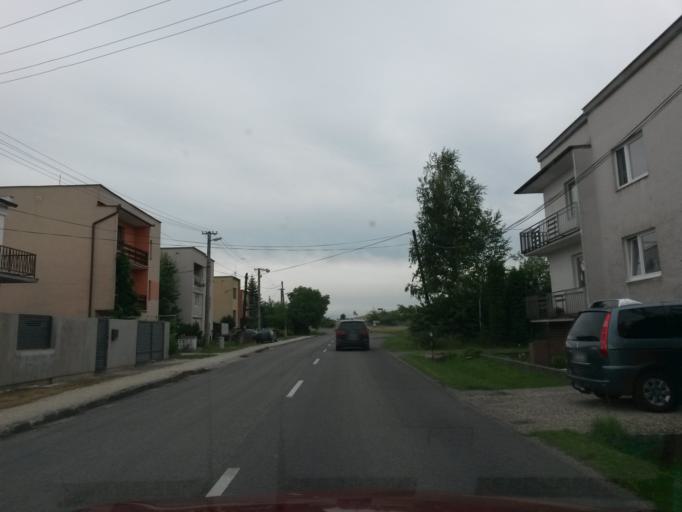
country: SK
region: Banskobystricky
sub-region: Okres Banska Bystrica
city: Zvolen
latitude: 48.5721
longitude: 19.1955
